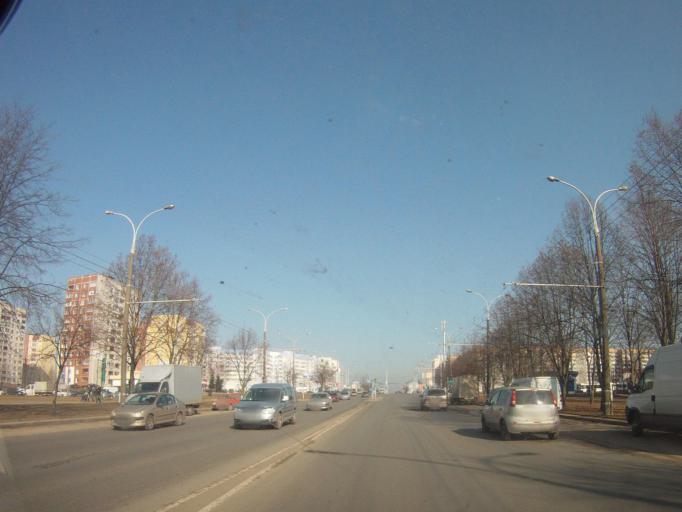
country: BY
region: Minsk
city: Novoye Medvezhino
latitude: 53.8988
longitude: 27.4350
